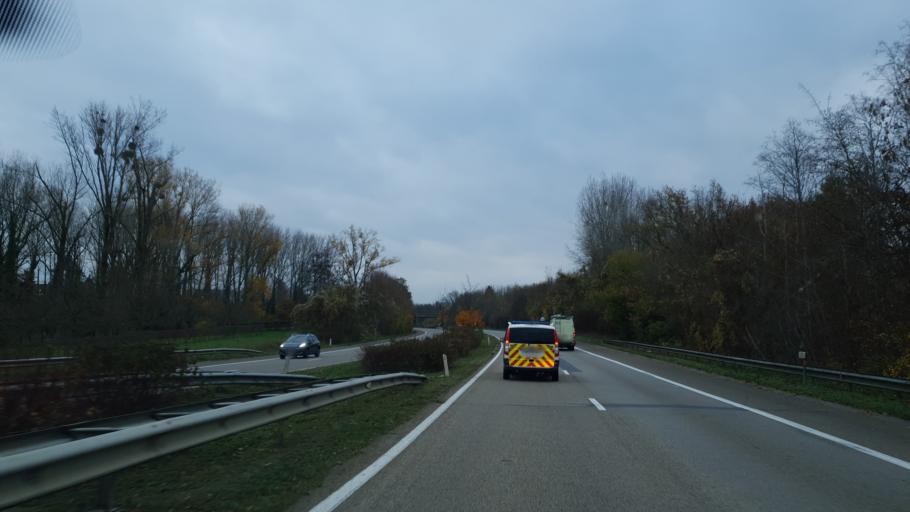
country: BE
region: Flanders
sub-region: Provincie Limburg
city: Bilzen
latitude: 50.8580
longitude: 5.5116
